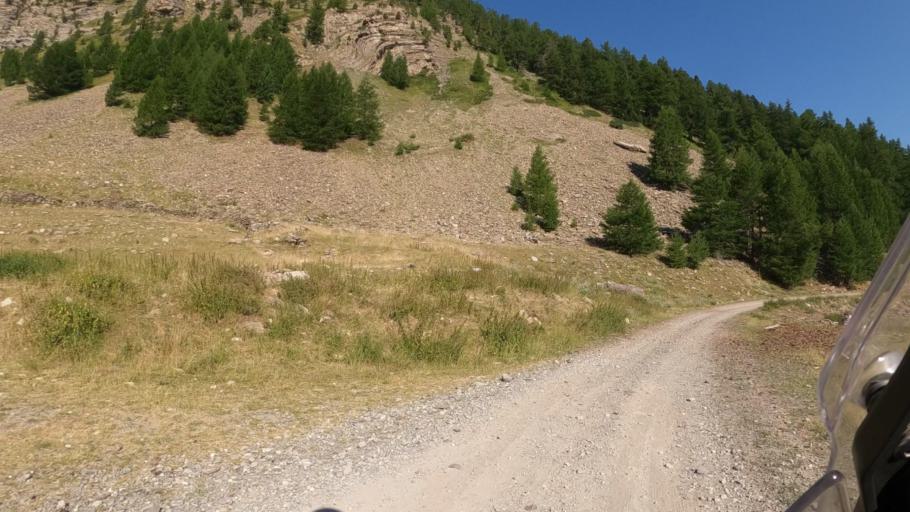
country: FR
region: Provence-Alpes-Cote d'Azur
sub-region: Departement des Hautes-Alpes
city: Guillestre
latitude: 44.5843
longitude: 6.5973
